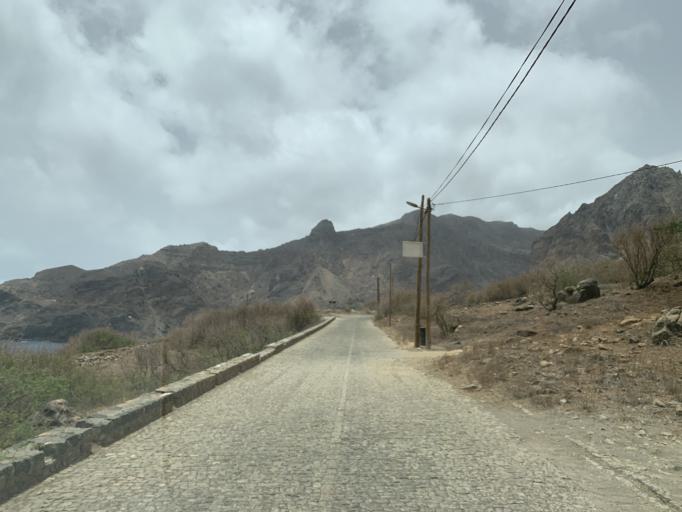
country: CV
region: Brava
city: Vila Nova Sintra
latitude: 14.8659
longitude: -24.7408
